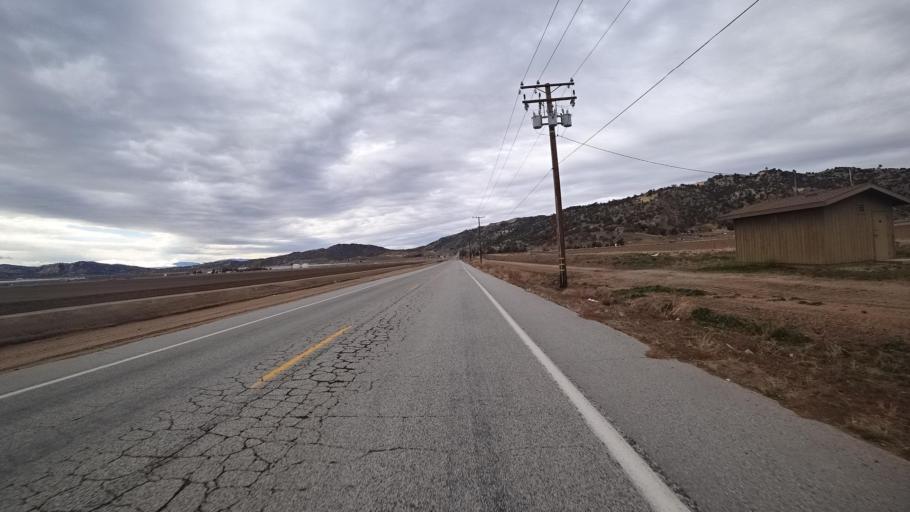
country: US
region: California
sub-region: Kern County
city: Bear Valley Springs
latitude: 35.1304
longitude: -118.5887
